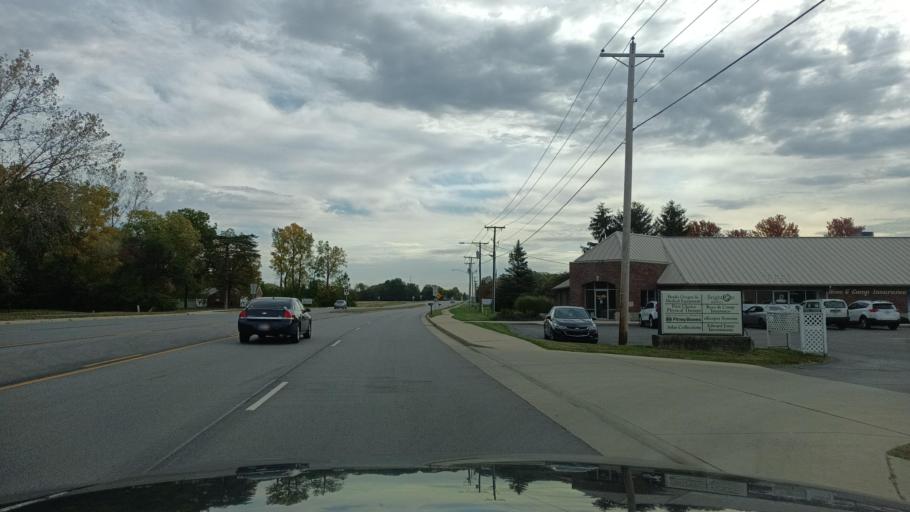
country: US
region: Indiana
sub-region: Delaware County
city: Yorktown
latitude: 40.1811
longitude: -85.4770
